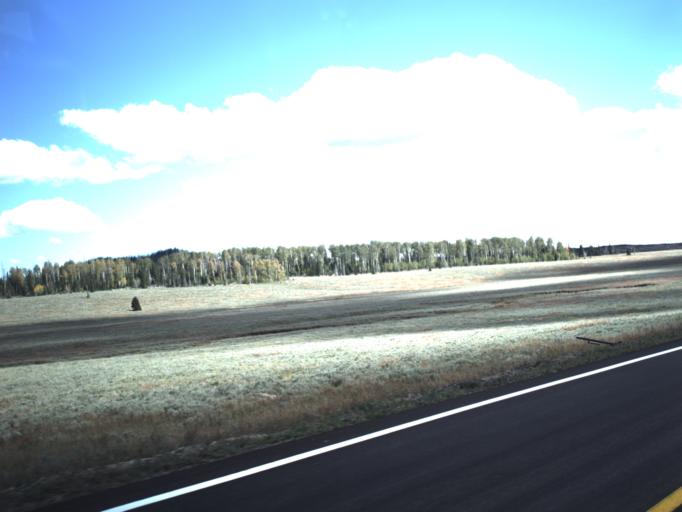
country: US
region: Utah
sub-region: Iron County
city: Parowan
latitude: 37.5667
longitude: -112.7901
